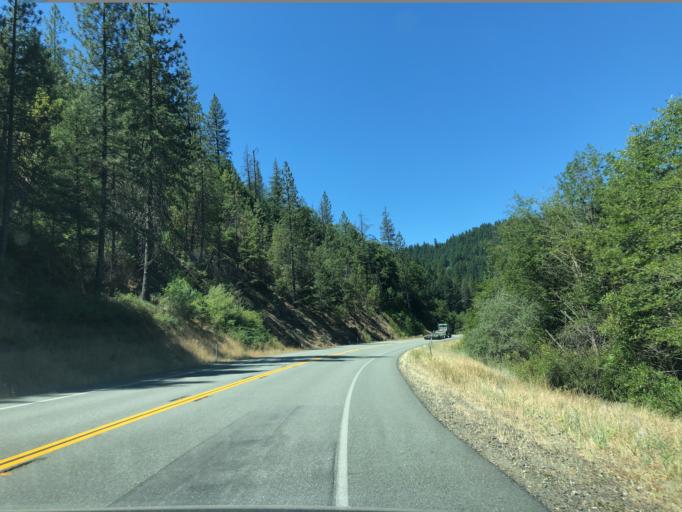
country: US
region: California
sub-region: Trinity County
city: Weaverville
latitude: 40.6825
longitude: -122.9360
